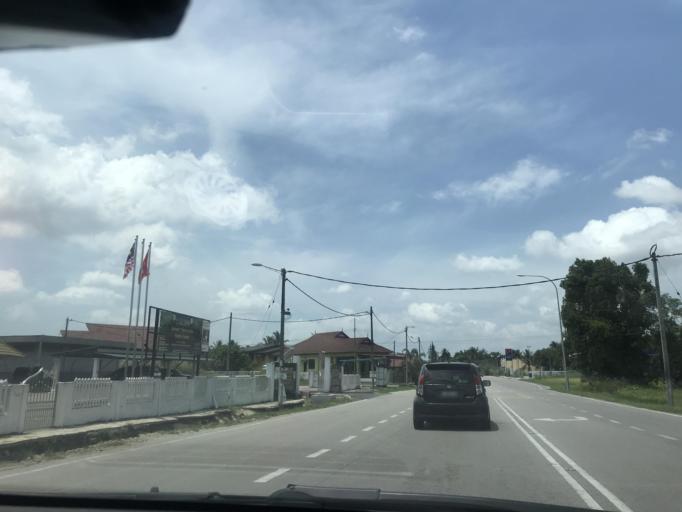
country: MY
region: Kelantan
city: Kota Bharu
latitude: 6.1561
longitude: 102.2020
